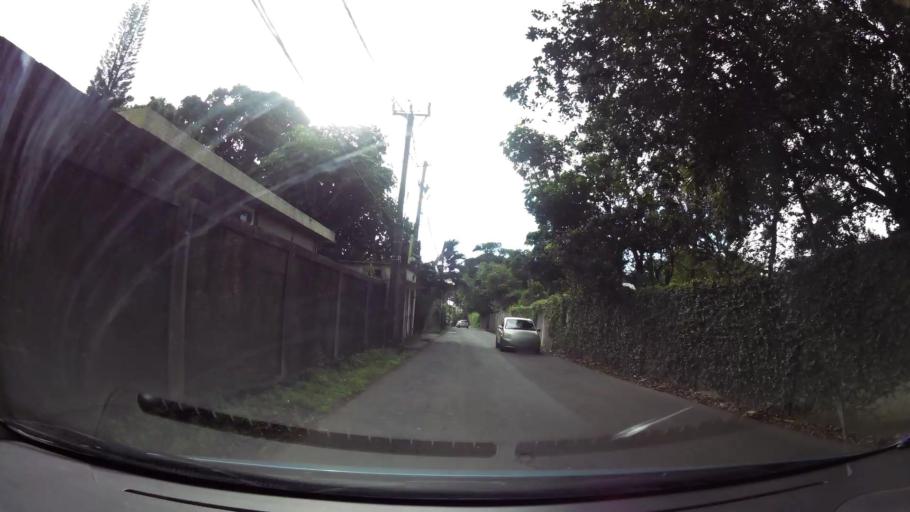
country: MU
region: Plaines Wilhems
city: Curepipe
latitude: -20.3243
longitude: 57.5215
